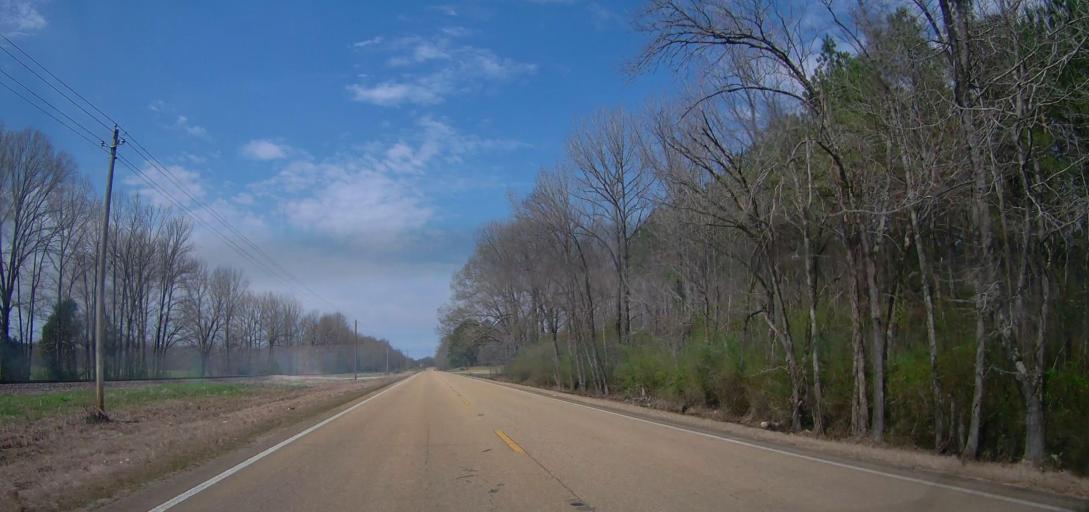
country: US
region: Mississippi
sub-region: Benton County
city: Ashland
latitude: 34.6275
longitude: -89.2621
